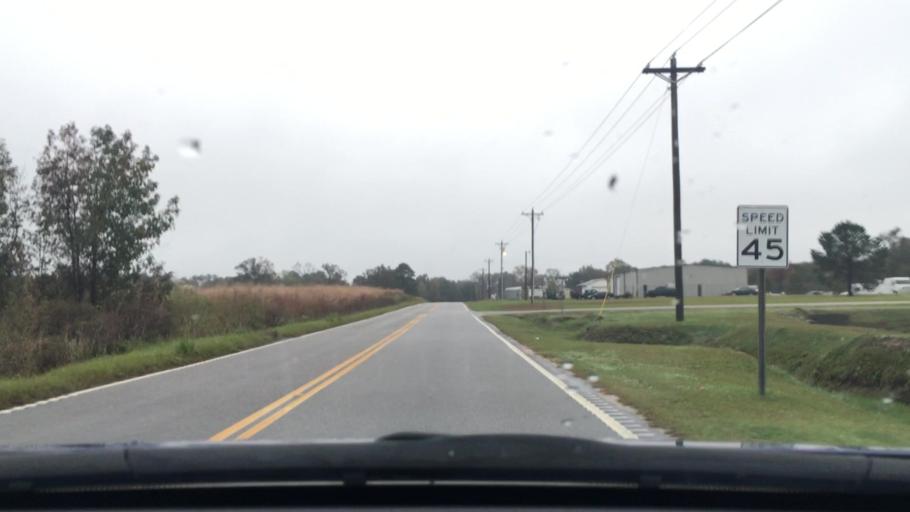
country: US
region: South Carolina
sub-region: Darlington County
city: Darlington
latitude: 34.2987
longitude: -79.9226
